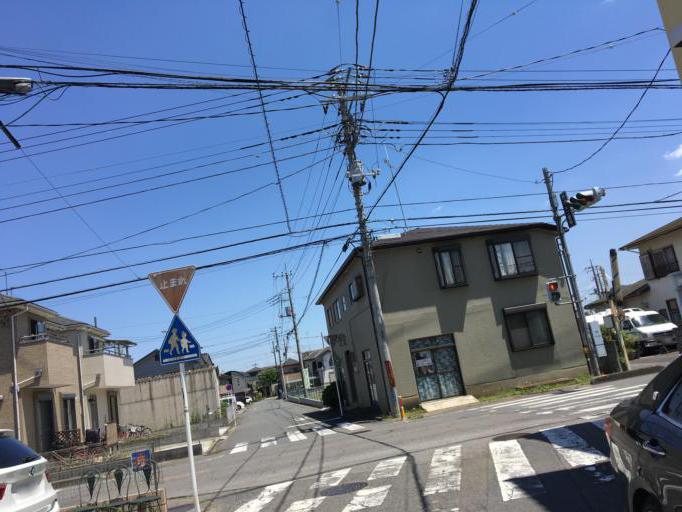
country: JP
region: Saitama
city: Sakado
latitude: 35.9461
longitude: 139.3869
